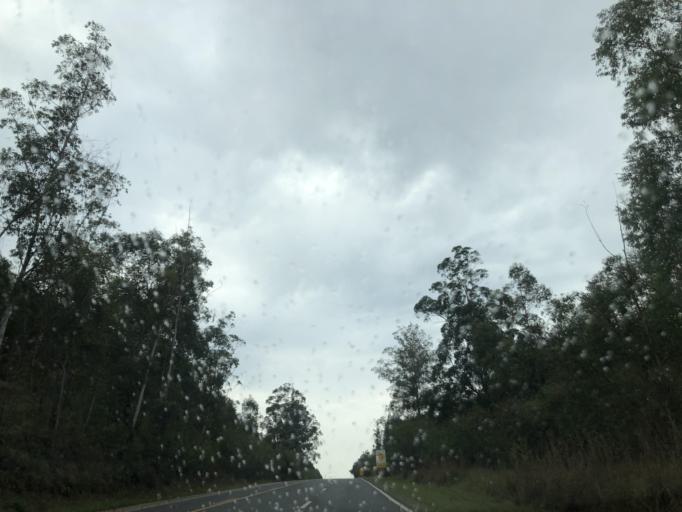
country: BR
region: Sao Paulo
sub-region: Salto De Pirapora
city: Salto de Pirapora
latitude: -23.6749
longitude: -47.6028
